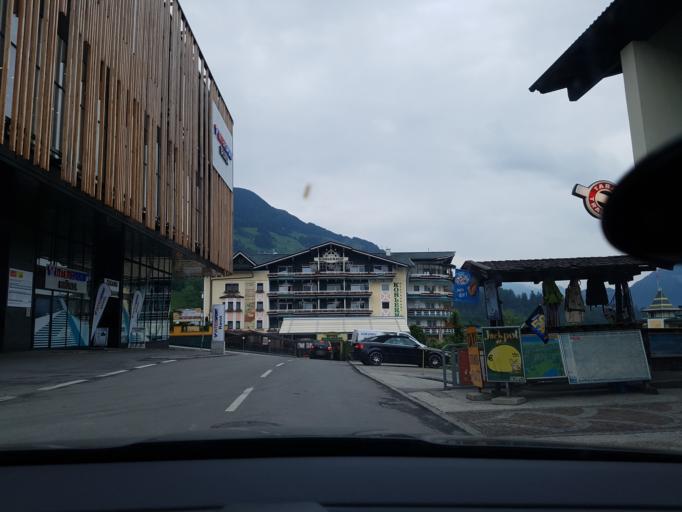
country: AT
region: Tyrol
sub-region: Politischer Bezirk Schwaz
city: Fugen
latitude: 47.3388
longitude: 11.8438
